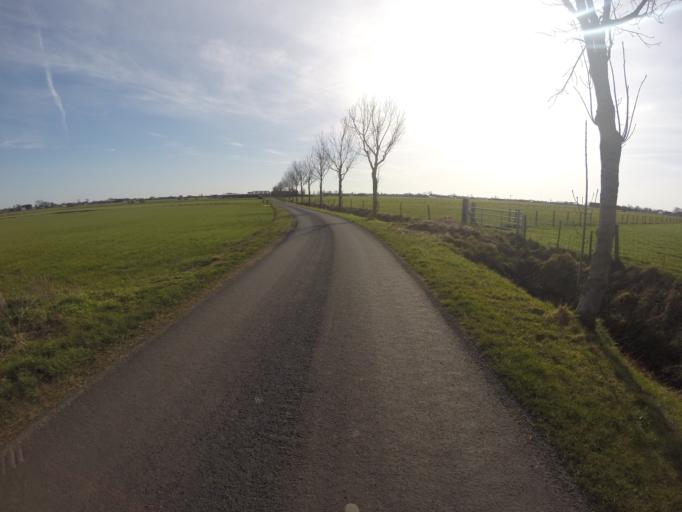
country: BE
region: Flanders
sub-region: Provincie West-Vlaanderen
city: Wingene
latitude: 51.0817
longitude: 3.2672
